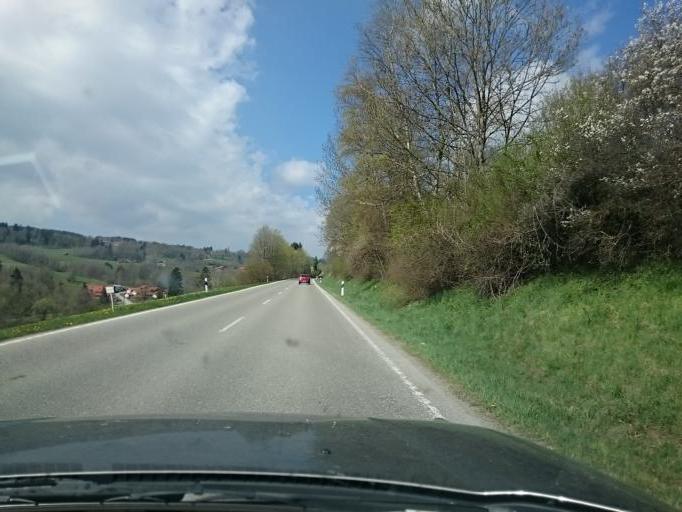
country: DE
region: Bavaria
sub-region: Upper Bavaria
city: Bad Kohlgrub
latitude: 47.6670
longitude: 11.0707
